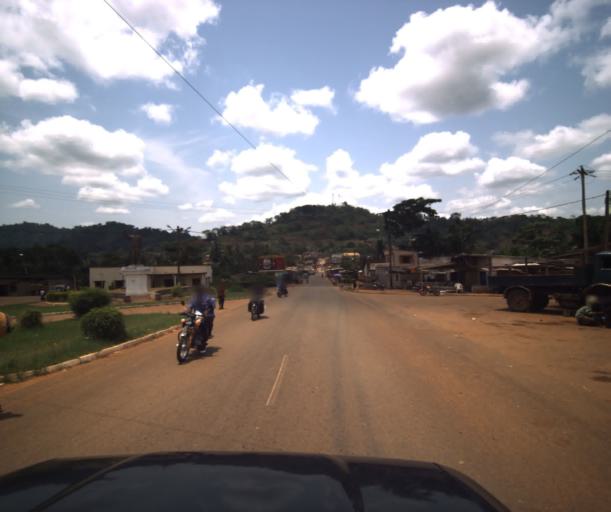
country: CM
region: Centre
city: Eseka
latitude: 3.6429
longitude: 10.7789
